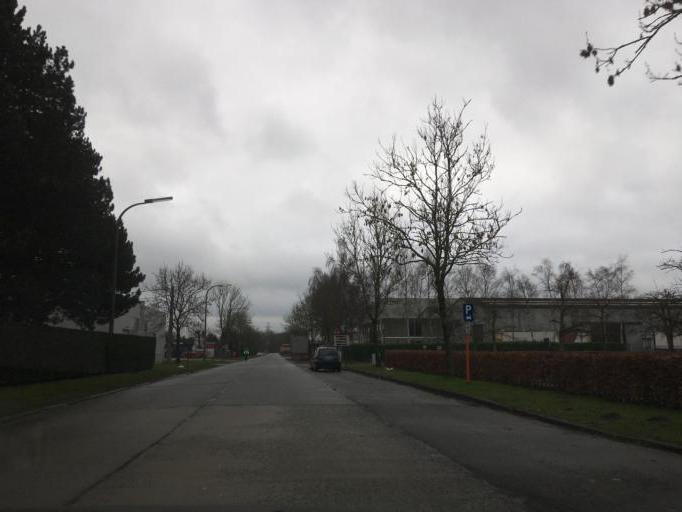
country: BE
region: Flanders
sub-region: Provincie West-Vlaanderen
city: Roeselare
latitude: 50.9767
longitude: 3.1302
